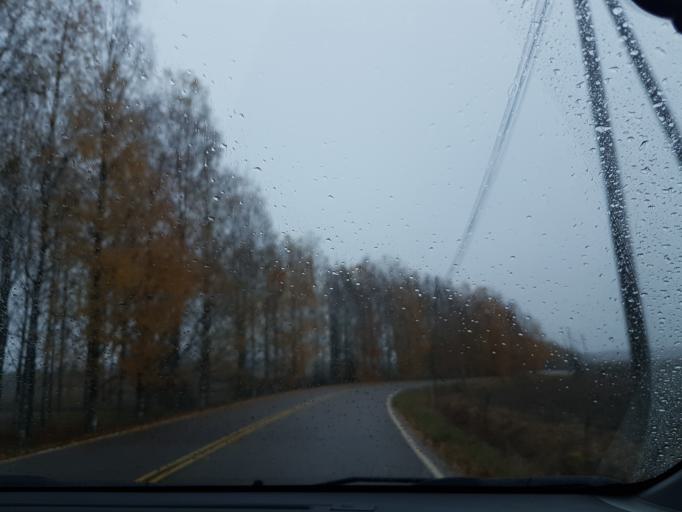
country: FI
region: Uusimaa
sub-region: Helsinki
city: Maentsaelae
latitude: 60.6149
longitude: 25.2311
